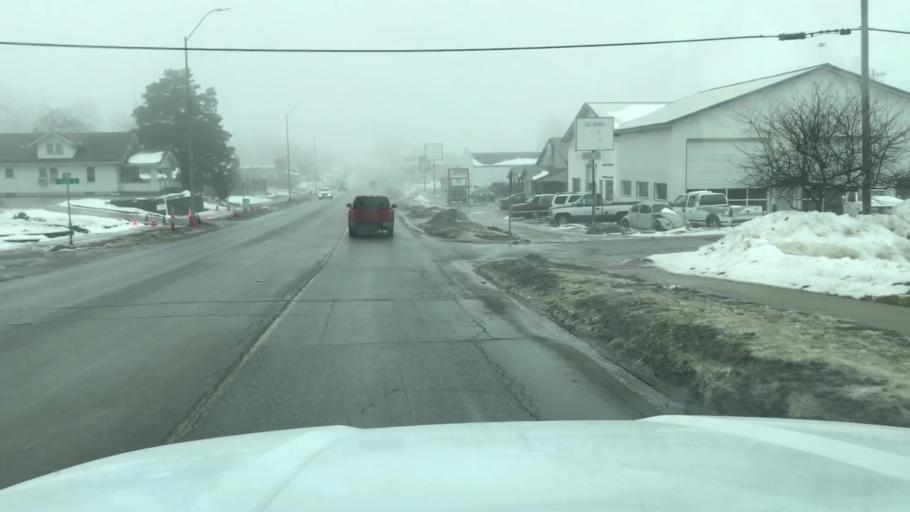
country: US
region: Missouri
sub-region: Clinton County
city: Cameron
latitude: 39.7432
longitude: -94.2357
